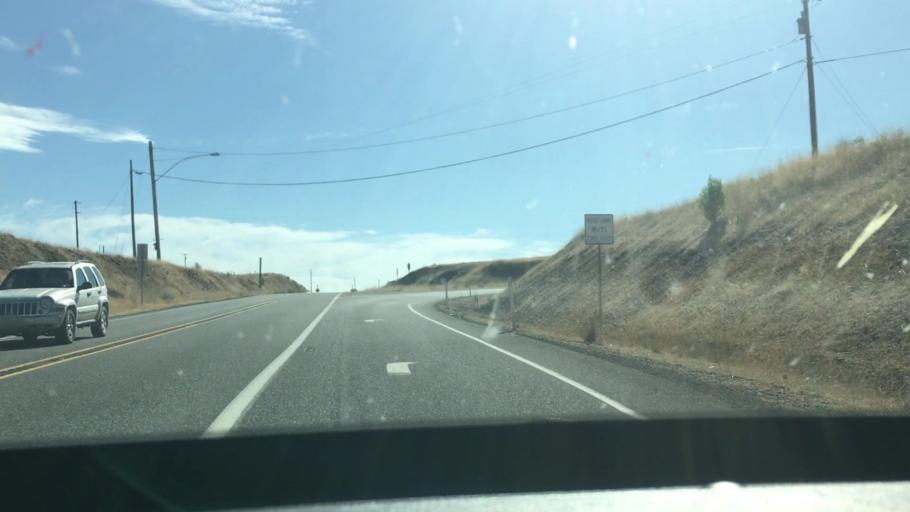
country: US
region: Washington
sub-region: Klickitat County
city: Goldendale
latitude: 45.6966
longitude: -120.8232
